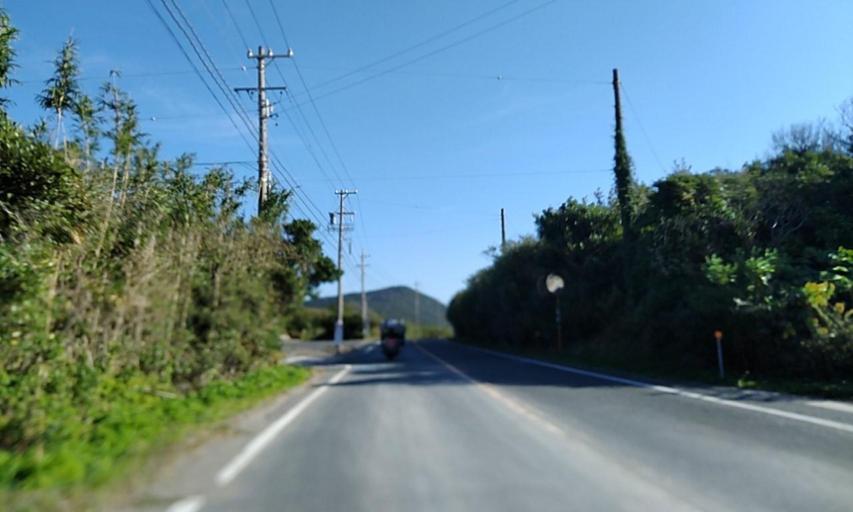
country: JP
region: Aichi
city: Toyohama
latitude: 34.5827
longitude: 137.0488
